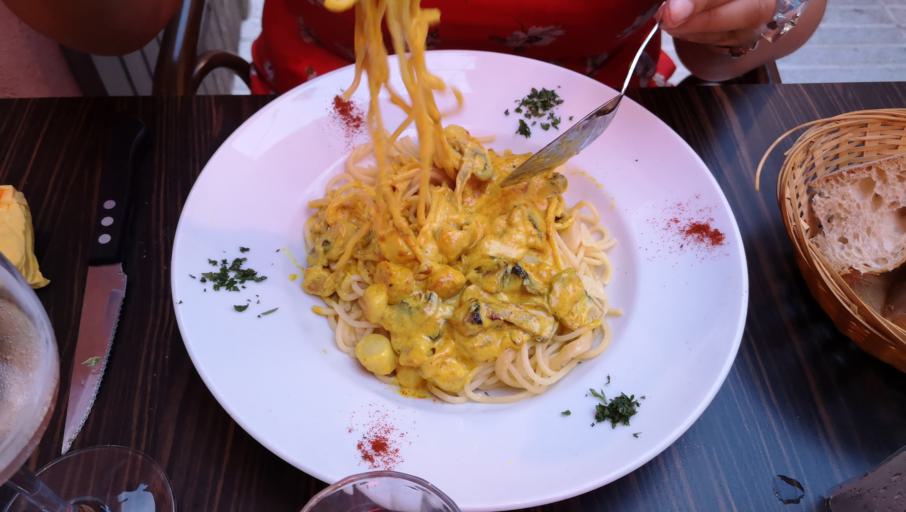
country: FR
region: Languedoc-Roussillon
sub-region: Departement des Pyrenees-Orientales
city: Banyuls de la Marenda
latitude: 42.4831
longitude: 3.1286
